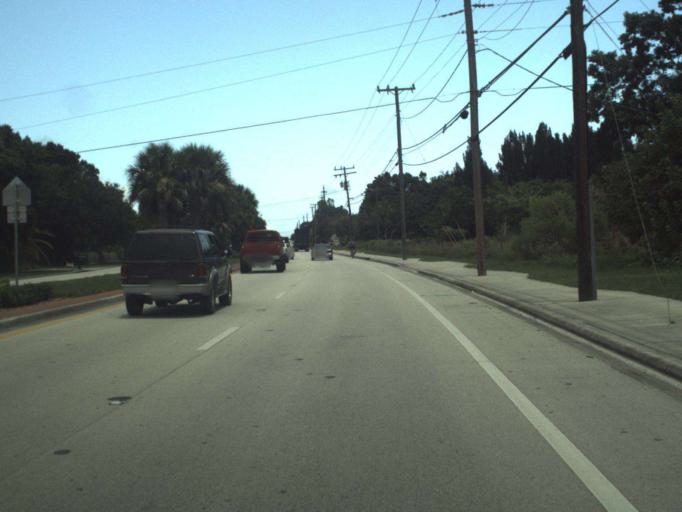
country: US
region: Florida
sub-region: Indian River County
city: Wabasso Beach
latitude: 27.7554
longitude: -80.4371
